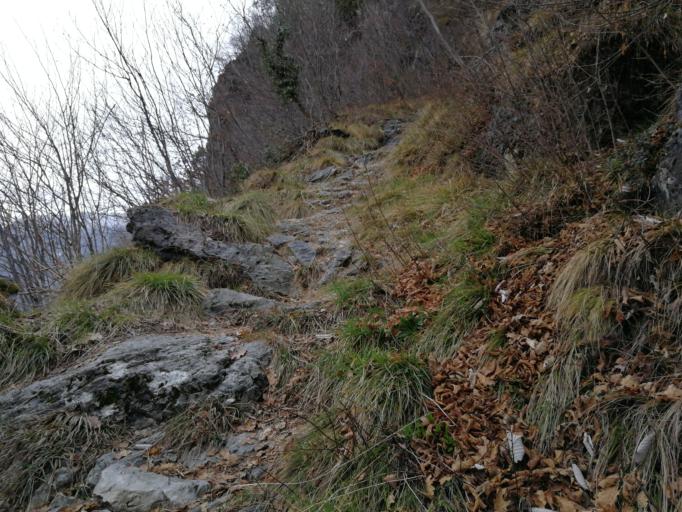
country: IT
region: Trentino-Alto Adige
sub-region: Provincia di Trento
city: Storo
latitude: 45.8482
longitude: 10.5941
